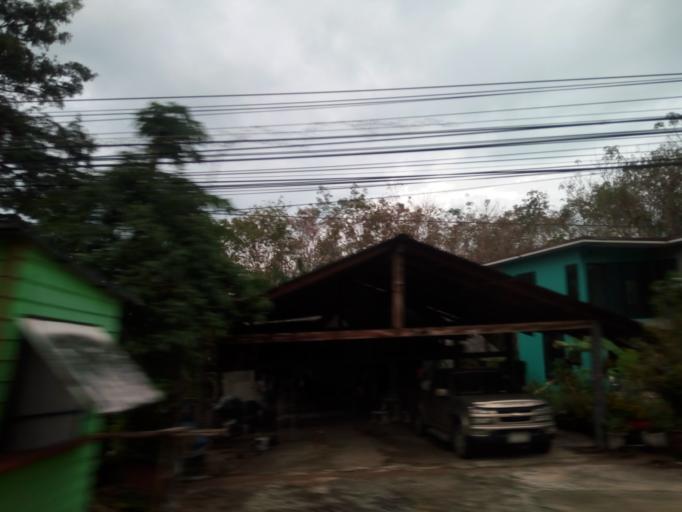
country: TH
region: Phuket
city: Thalang
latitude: 8.0887
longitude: 98.3641
